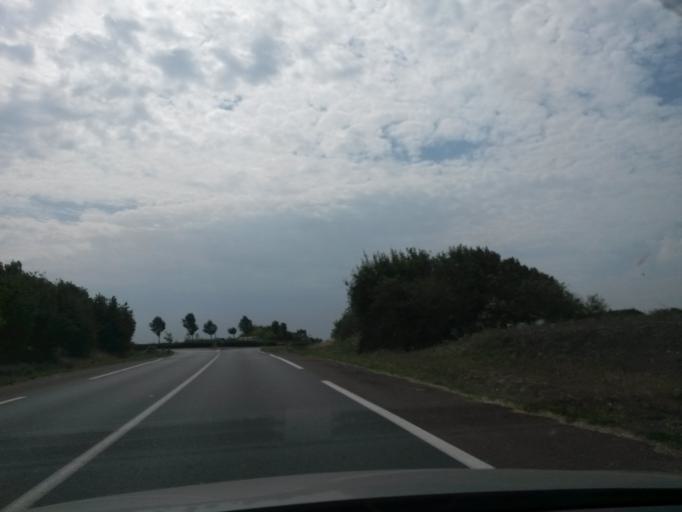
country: FR
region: Poitou-Charentes
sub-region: Departement de la Charente-Maritime
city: Saint-Xandre
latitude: 46.1964
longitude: -1.0954
